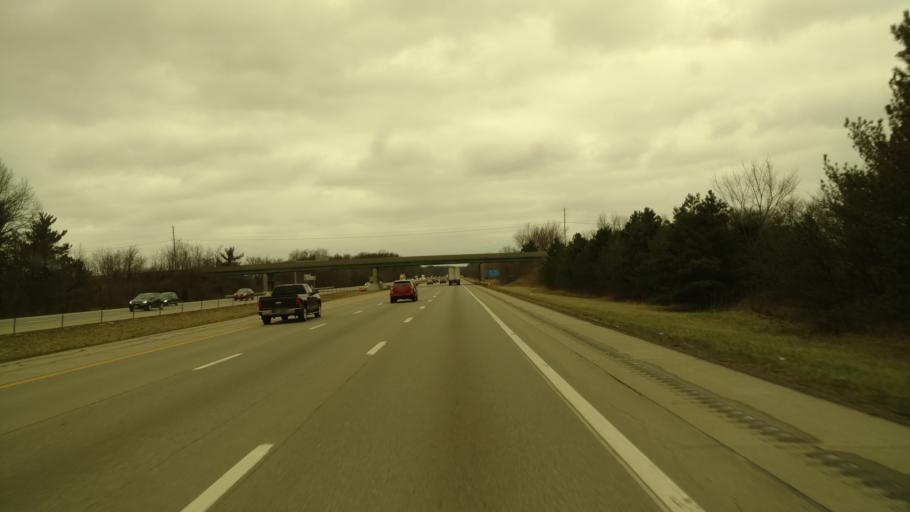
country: US
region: Ohio
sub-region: Delaware County
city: Sunbury
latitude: 40.2831
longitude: -82.9256
